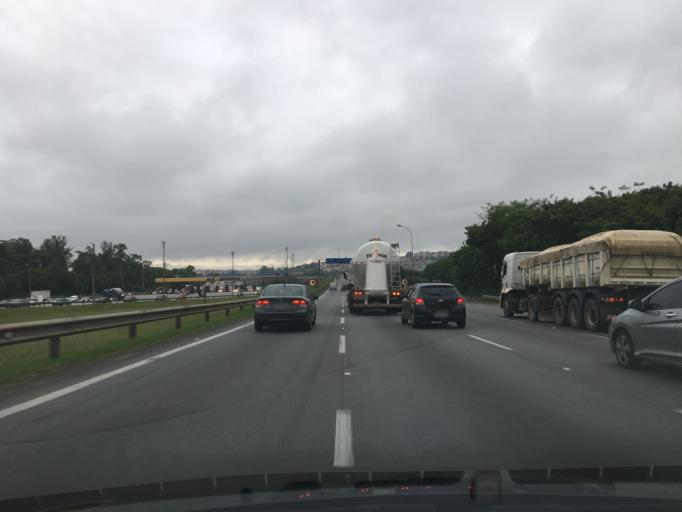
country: BR
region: Sao Paulo
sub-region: Carapicuiba
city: Carapicuiba
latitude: -23.5151
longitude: -46.8122
